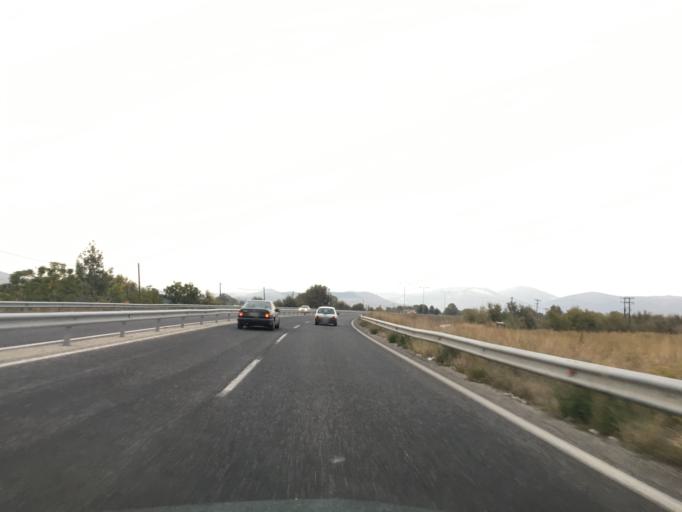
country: GR
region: Thessaly
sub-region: Trikala
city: Trikala
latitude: 39.5612
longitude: 21.8022
